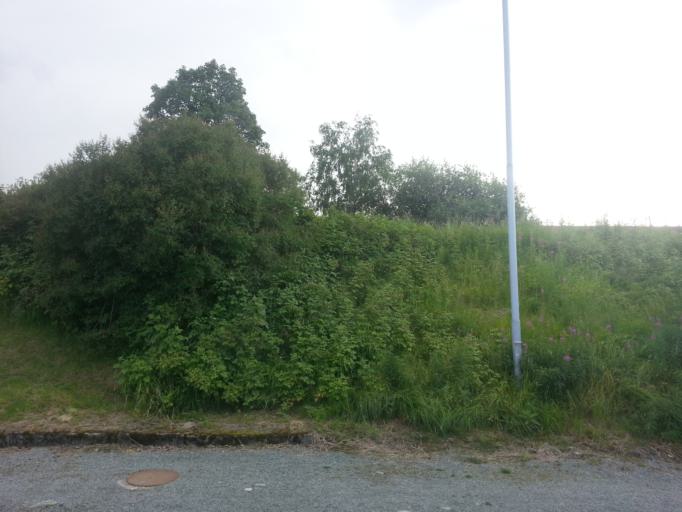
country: NO
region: Sor-Trondelag
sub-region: Trondheim
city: Trondheim
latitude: 63.4369
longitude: 10.4640
